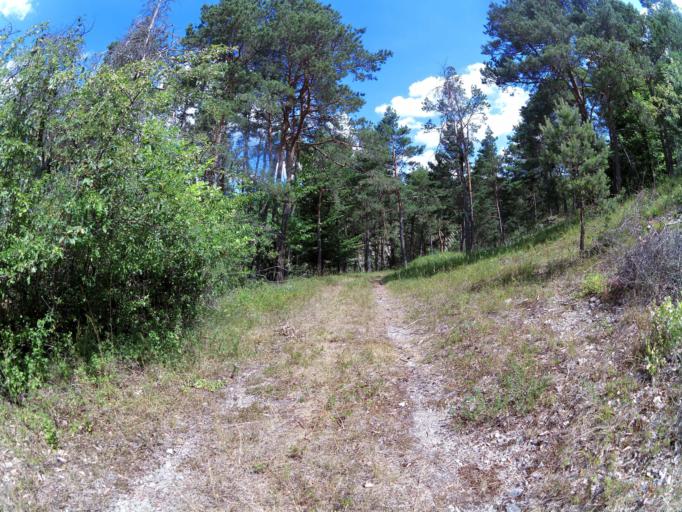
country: DE
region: Bavaria
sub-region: Regierungsbezirk Unterfranken
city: Thungersheim
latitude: 49.8916
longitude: 9.8438
